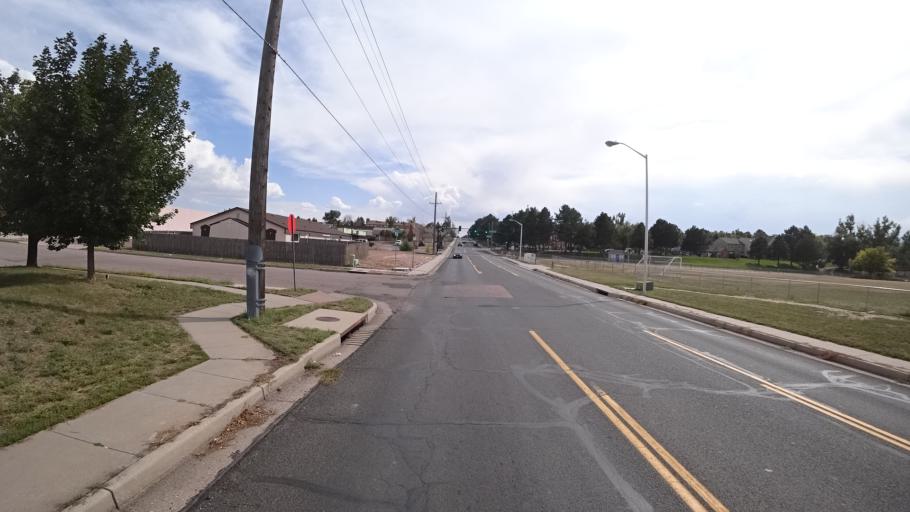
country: US
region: Colorado
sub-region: El Paso County
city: Cimarron Hills
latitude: 38.8869
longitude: -104.7609
